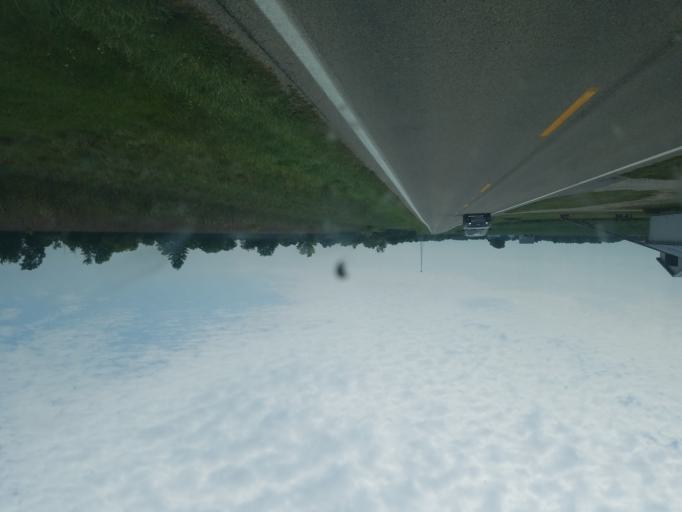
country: US
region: Ohio
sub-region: Marion County
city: Marion
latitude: 40.5686
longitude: -83.2179
